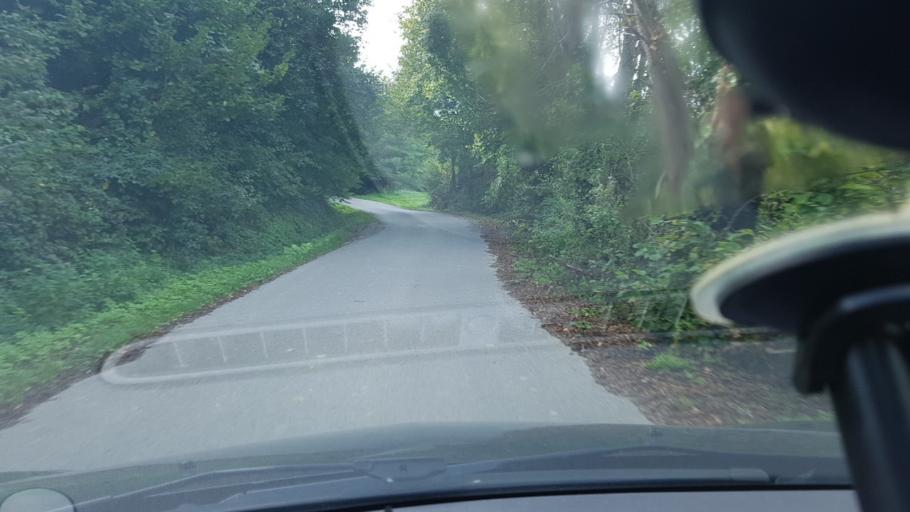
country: HR
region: Krapinsko-Zagorska
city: Radoboj
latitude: 46.1771
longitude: 15.9612
